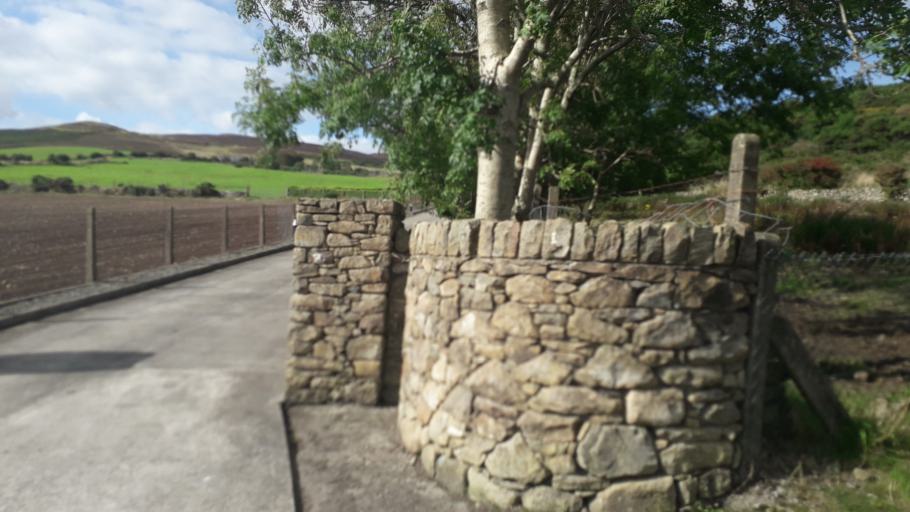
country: GB
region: Northern Ireland
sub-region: Down District
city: Warrenpoint
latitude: 54.0315
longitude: -6.2818
